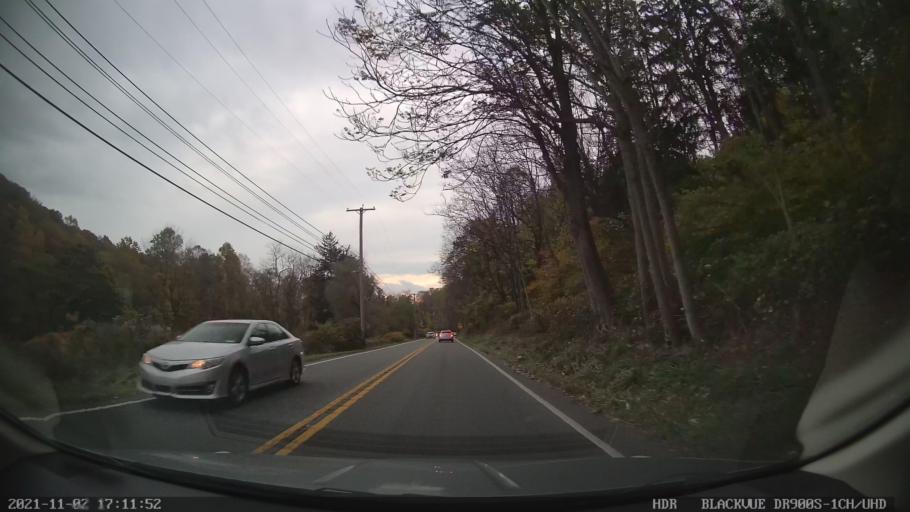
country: US
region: Pennsylvania
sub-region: Berks County
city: South Temple
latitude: 40.3893
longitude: -75.8807
